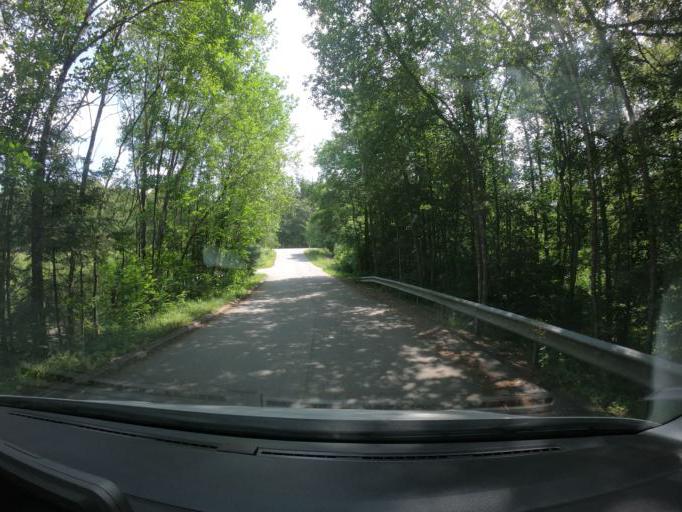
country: SE
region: Skane
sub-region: Hassleholms Kommun
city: Sosdala
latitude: 55.9848
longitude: 13.6041
